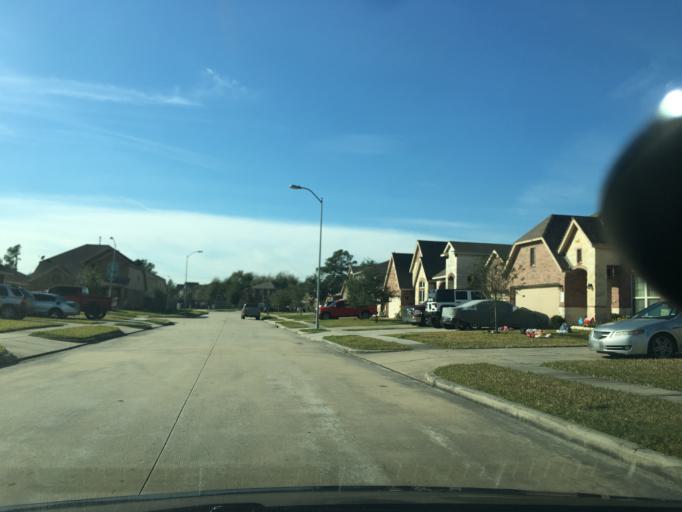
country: US
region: Texas
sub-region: Harris County
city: Cloverleaf
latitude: 29.8155
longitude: -95.1598
